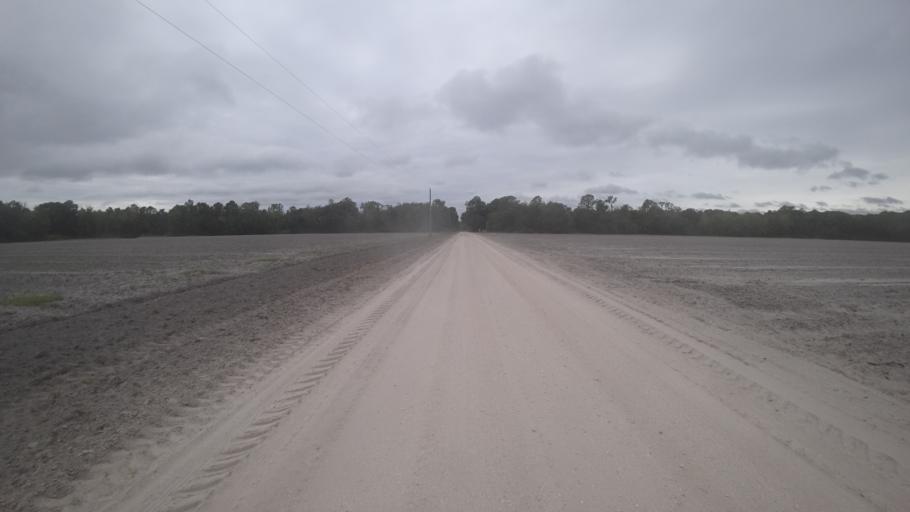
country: US
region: Florida
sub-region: Hillsborough County
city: Wimauma
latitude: 27.5750
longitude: -82.1325
